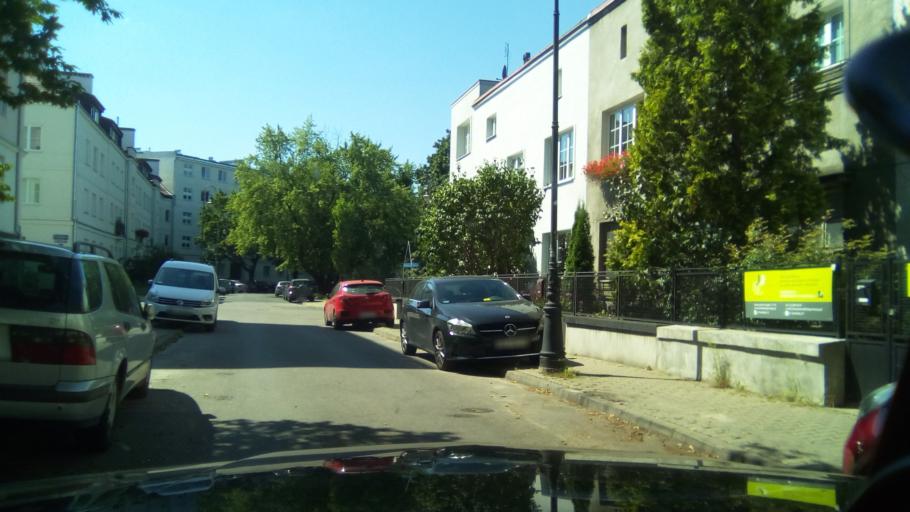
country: PL
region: Masovian Voivodeship
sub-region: Warszawa
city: Zoliborz
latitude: 52.2705
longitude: 20.9888
